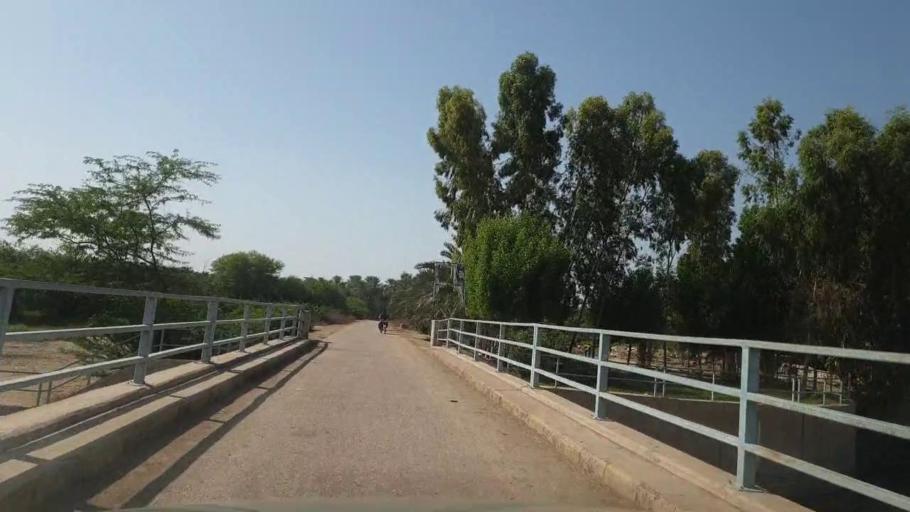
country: PK
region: Sindh
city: Rohri
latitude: 27.6322
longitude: 68.9071
